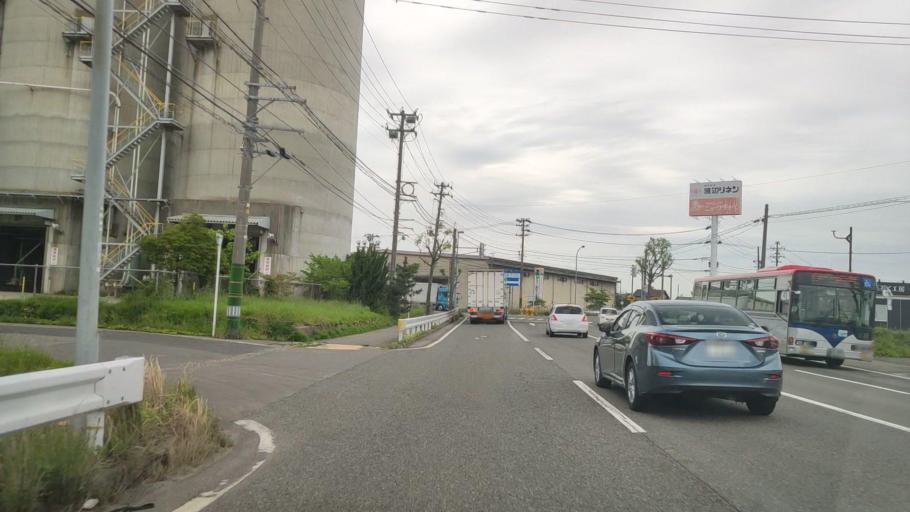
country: JP
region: Niigata
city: Niigata-shi
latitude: 37.9309
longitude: 139.0689
